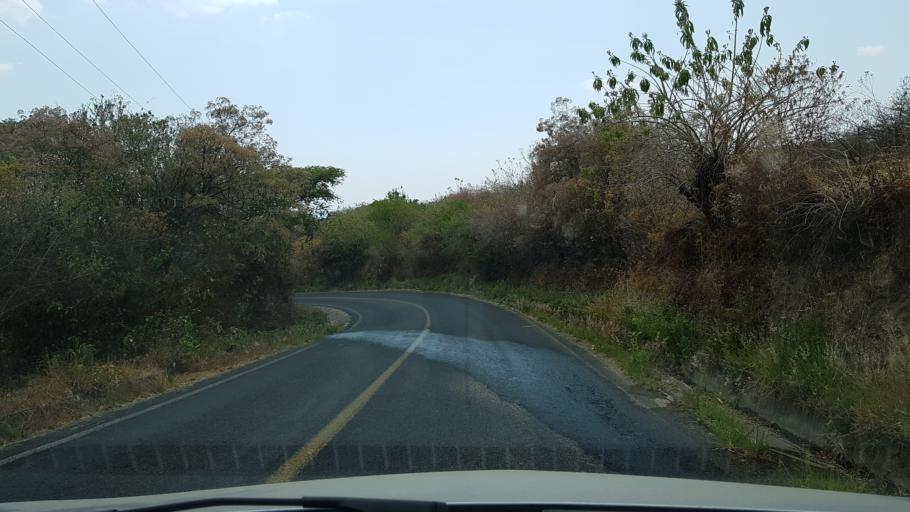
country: MX
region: Puebla
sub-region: Tochimilco
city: San Antonio Alpanocan
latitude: 18.8384
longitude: -98.7205
